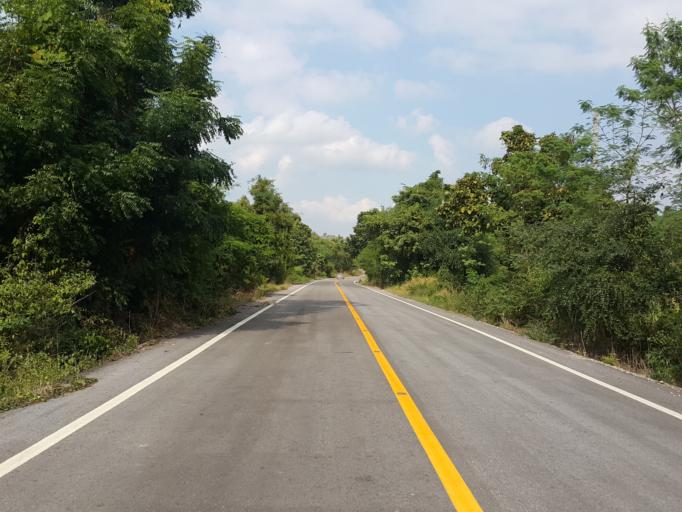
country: TH
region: Sukhothai
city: Thung Saliam
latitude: 17.4396
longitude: 99.5881
